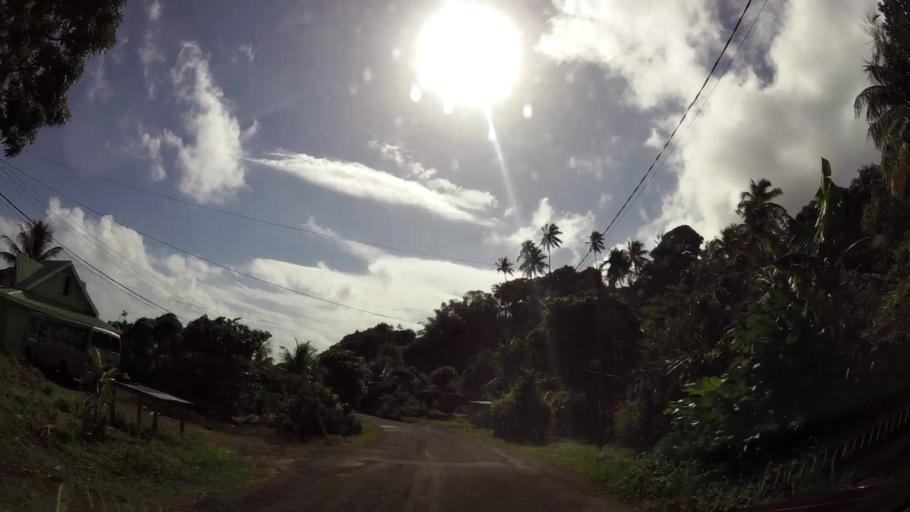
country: DM
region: Saint David
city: Castle Bruce
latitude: 15.4807
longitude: -61.2531
